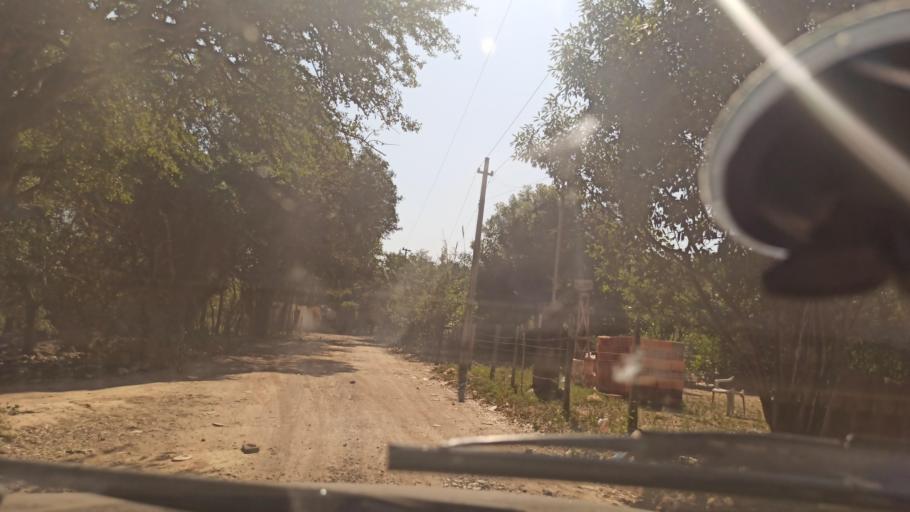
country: AR
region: Formosa
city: Clorinda
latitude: -25.3060
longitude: -57.6986
